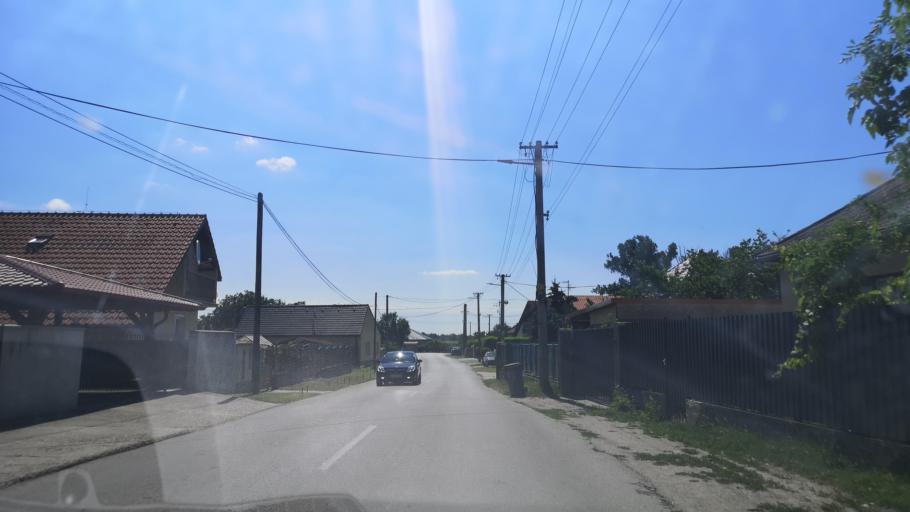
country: SK
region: Bratislavsky
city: Senec
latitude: 48.1004
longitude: 17.4774
